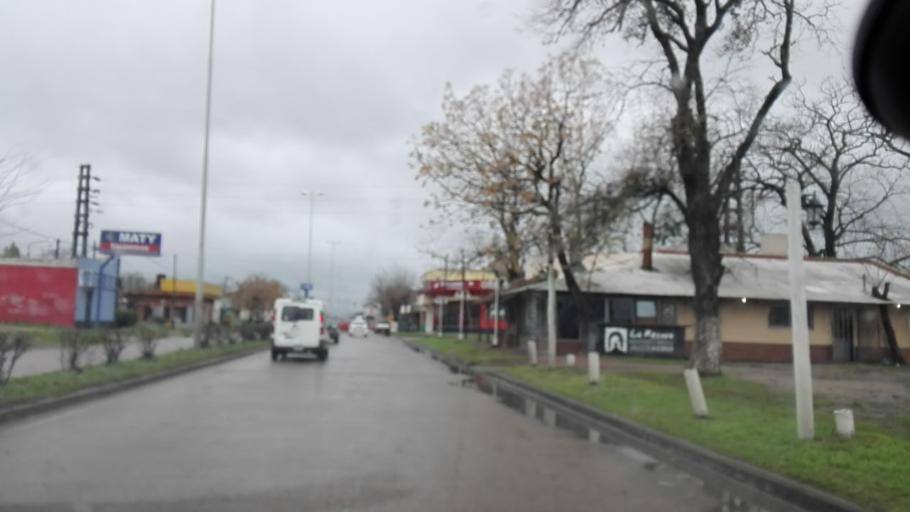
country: AR
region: Buenos Aires
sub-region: Partido de Brandsen
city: Brandsen
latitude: -35.1737
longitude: -58.2326
